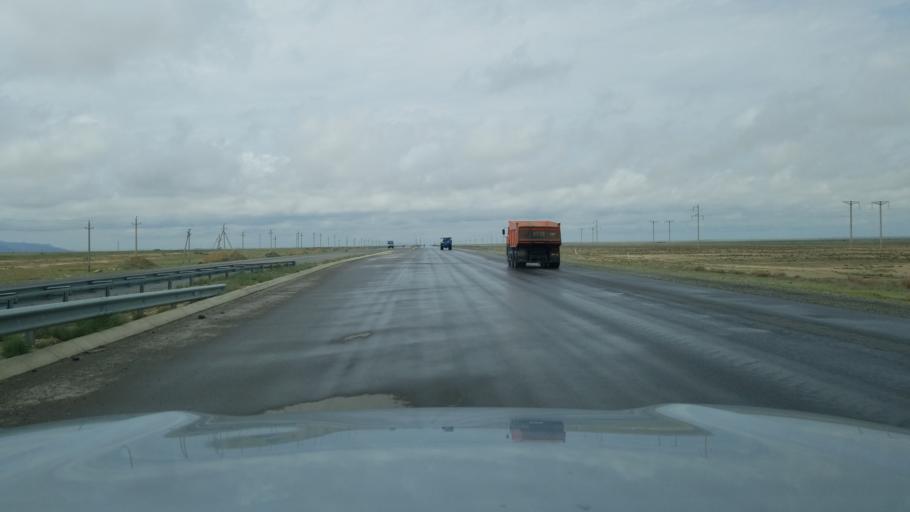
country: TM
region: Balkan
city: Gazanjyk
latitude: 39.1899
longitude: 55.7878
